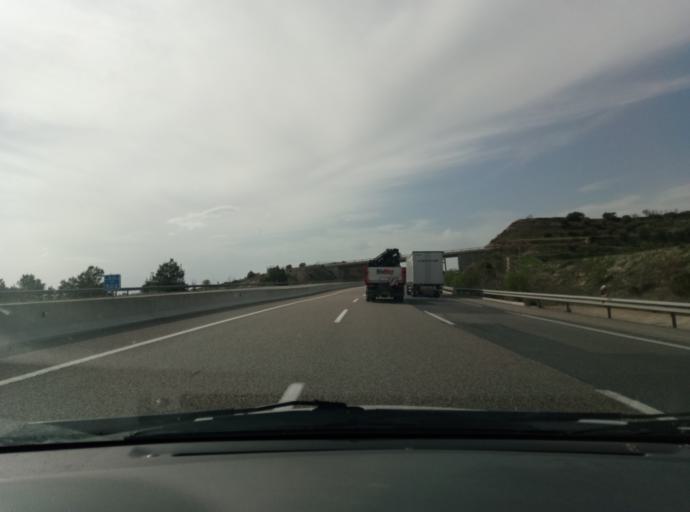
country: ES
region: Catalonia
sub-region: Provincia de Lleida
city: Cervera
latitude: 41.6667
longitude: 1.2971
